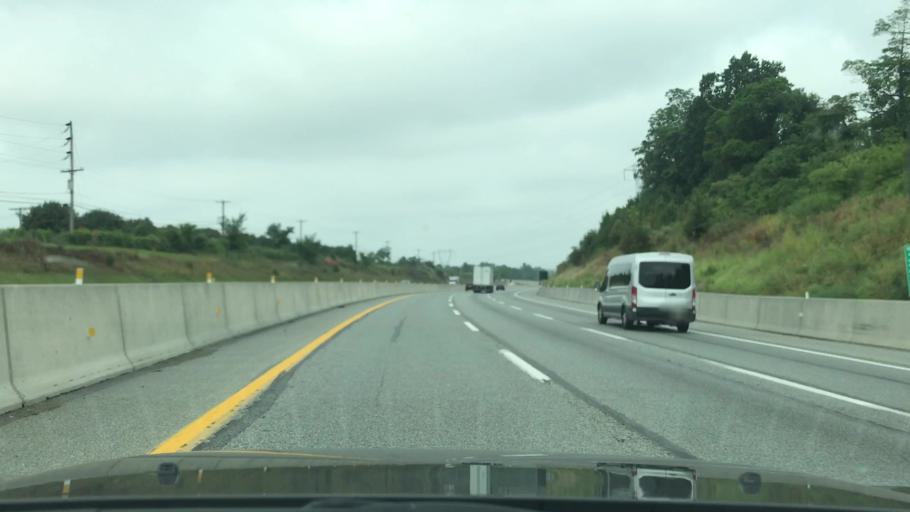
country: US
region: Pennsylvania
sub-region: Montgomery County
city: Bridgeport
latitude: 40.0874
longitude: -75.3618
